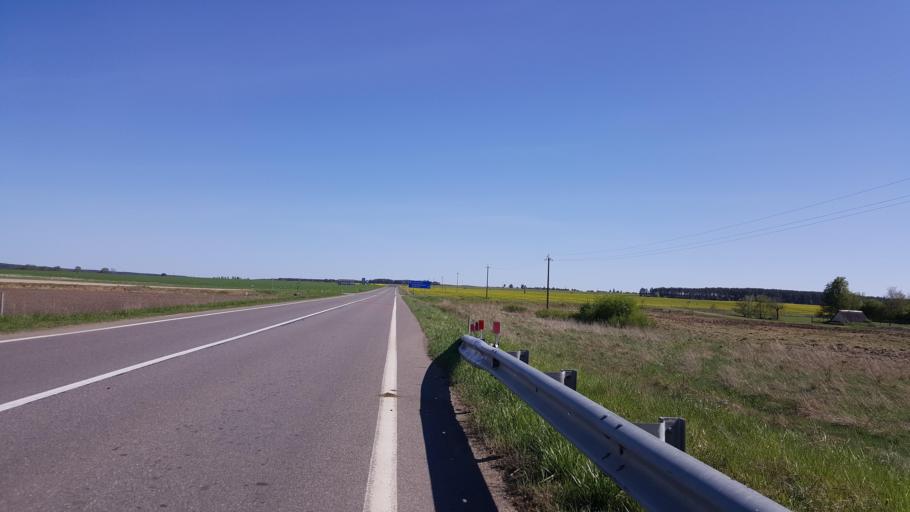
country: BY
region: Brest
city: Kamyanyets
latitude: 52.4218
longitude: 23.8418
